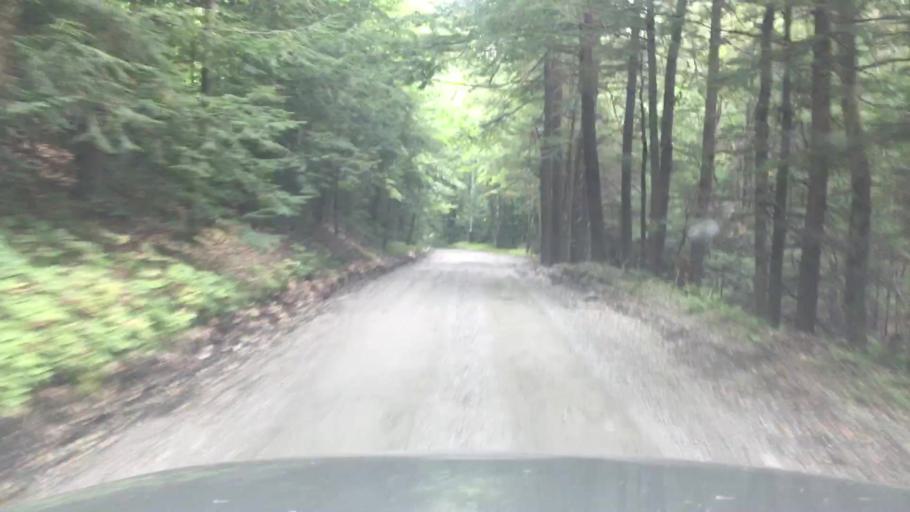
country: US
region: Vermont
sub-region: Windham County
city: Dover
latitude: 42.8335
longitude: -72.7684
